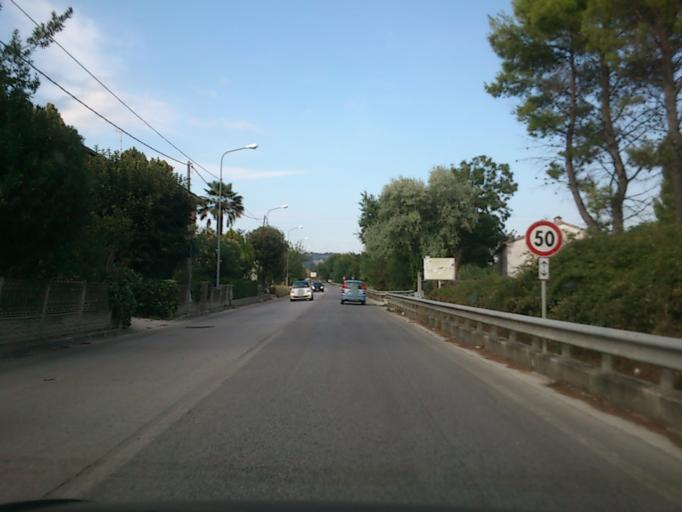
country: IT
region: The Marches
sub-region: Provincia di Pesaro e Urbino
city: Lucrezia
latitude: 43.7834
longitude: 12.9440
